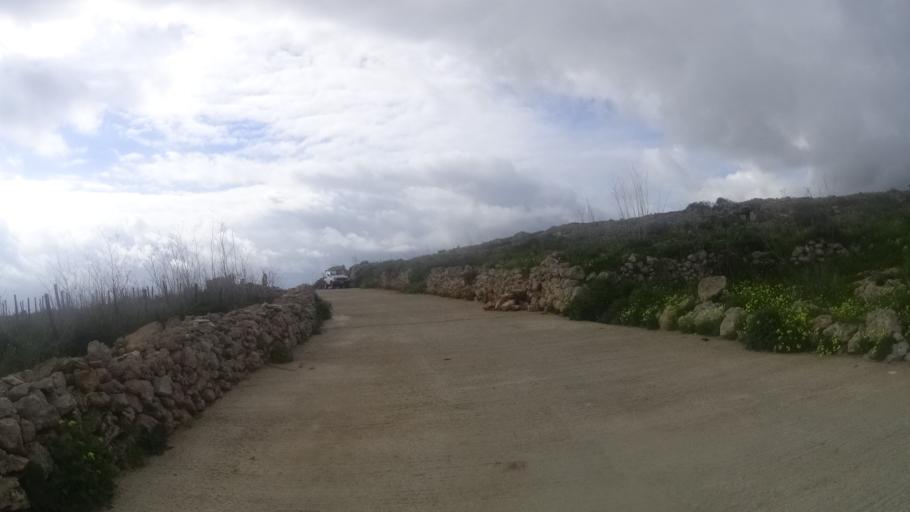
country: MT
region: Il-Qala
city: Qala
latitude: 36.0343
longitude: 14.3235
